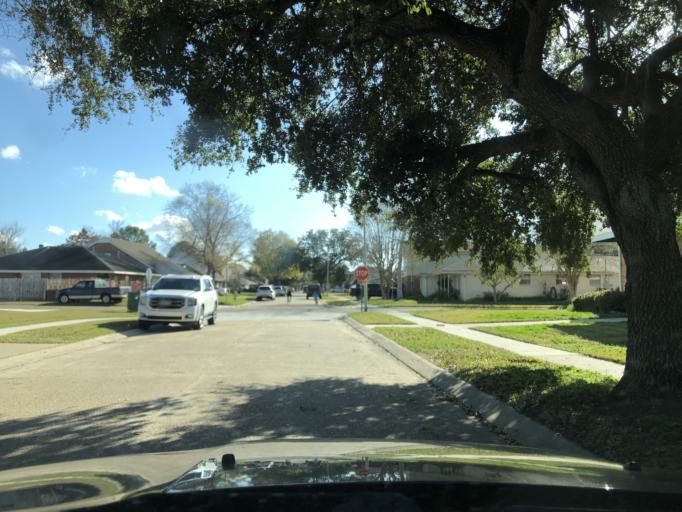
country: US
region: Louisiana
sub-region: Jefferson Parish
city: Metairie Terrace
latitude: 29.9907
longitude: -90.1663
